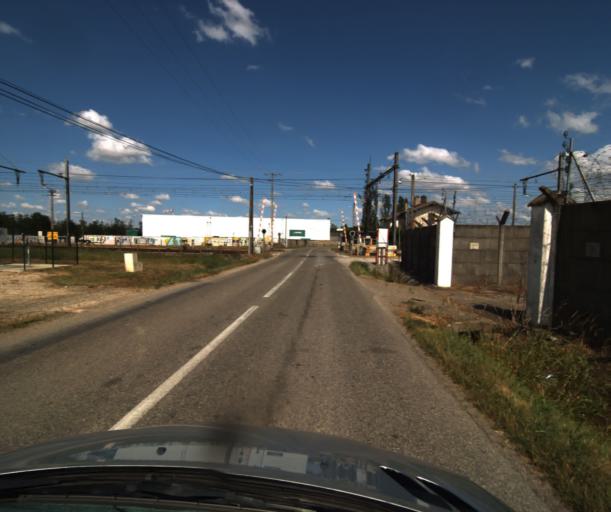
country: FR
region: Midi-Pyrenees
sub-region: Departement du Tarn-et-Garonne
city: Finhan
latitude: 43.9223
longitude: 1.2640
